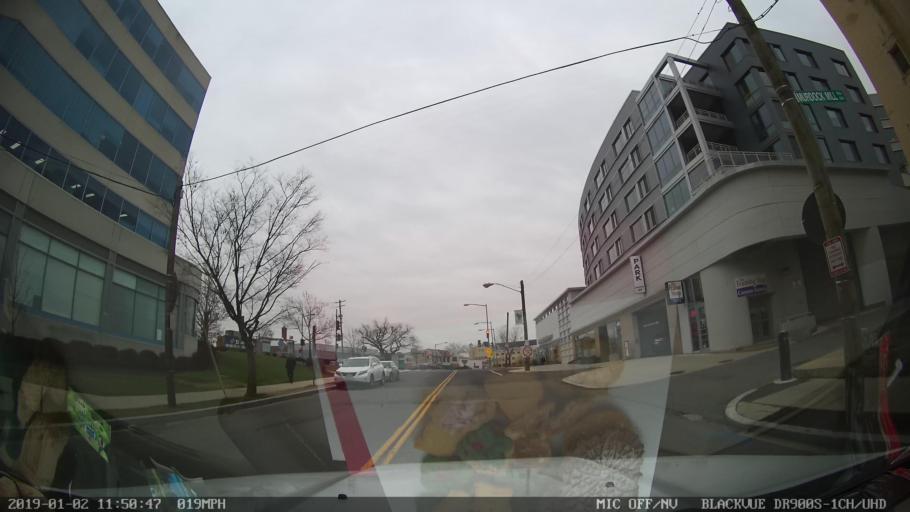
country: US
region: Maryland
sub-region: Montgomery County
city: Friendship Village
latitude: 38.9492
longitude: -77.0809
